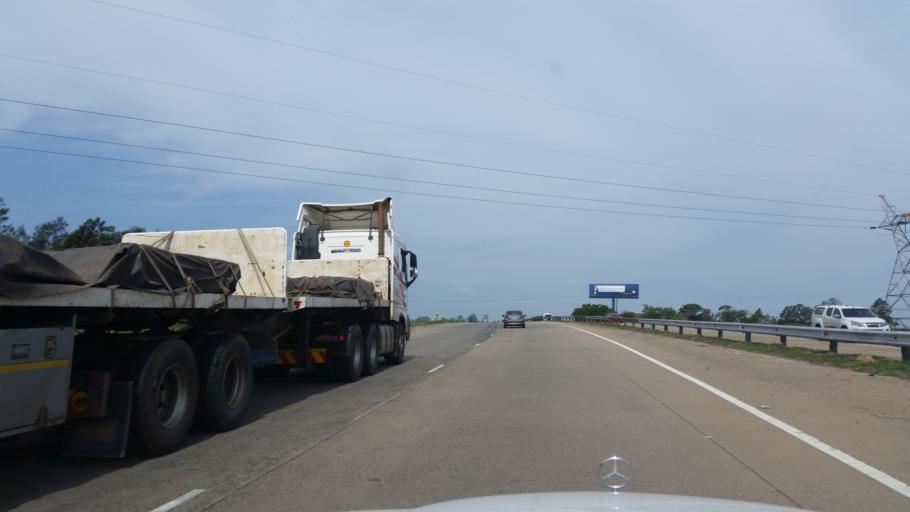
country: ZA
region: KwaZulu-Natal
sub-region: uMgungundlovu District Municipality
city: Camperdown
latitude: -29.7340
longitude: 30.5760
